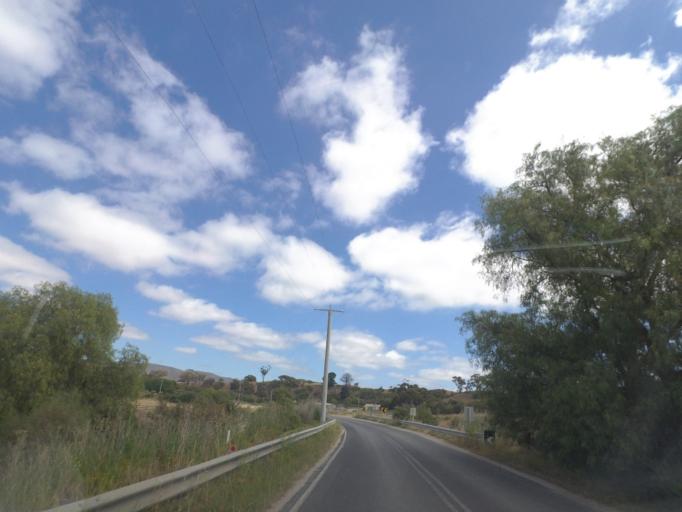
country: AU
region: Victoria
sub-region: Moorabool
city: Bacchus Marsh
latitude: -37.6473
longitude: 144.4488
